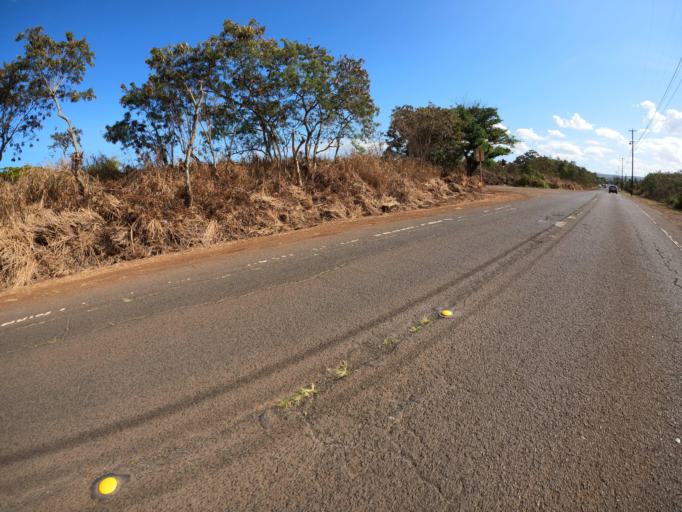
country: US
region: Hawaii
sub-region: Honolulu County
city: Waialua
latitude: 21.5696
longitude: -158.1361
